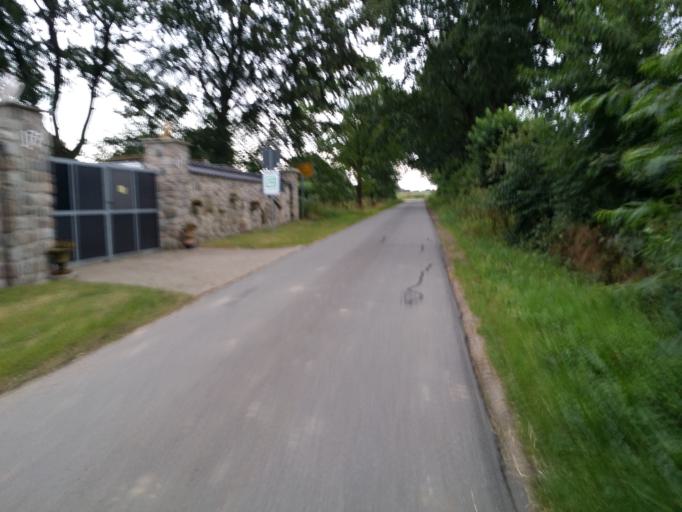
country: DE
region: Schleswig-Holstein
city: Nutteln
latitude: 53.9870
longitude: 9.3921
